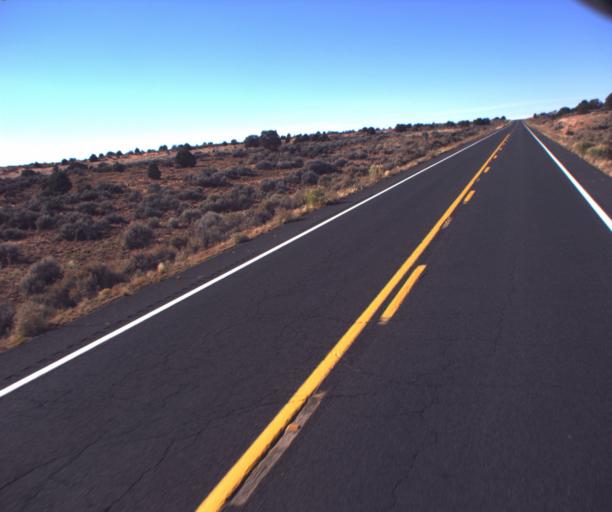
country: US
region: Arizona
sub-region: Coconino County
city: Kaibito
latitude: 36.5618
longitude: -110.7527
